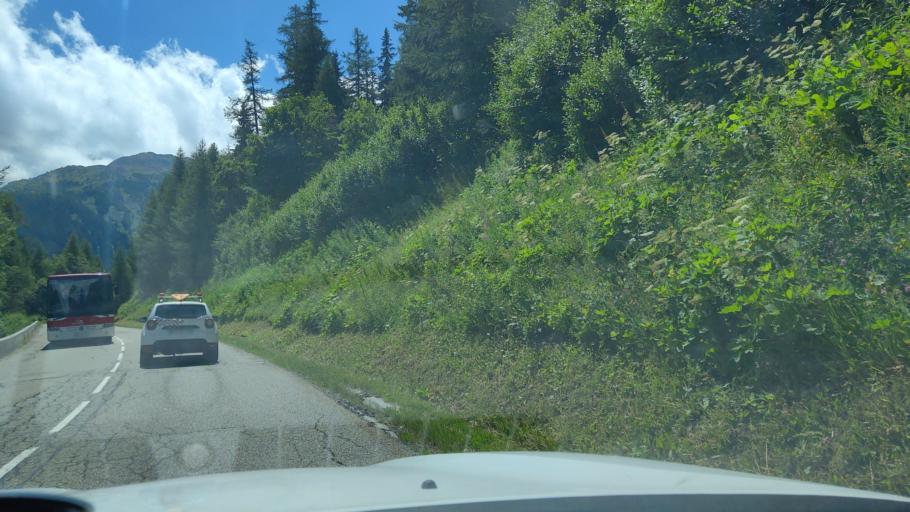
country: FR
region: Rhone-Alpes
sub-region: Departement de la Savoie
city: Seez
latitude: 45.5948
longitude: 6.8251
